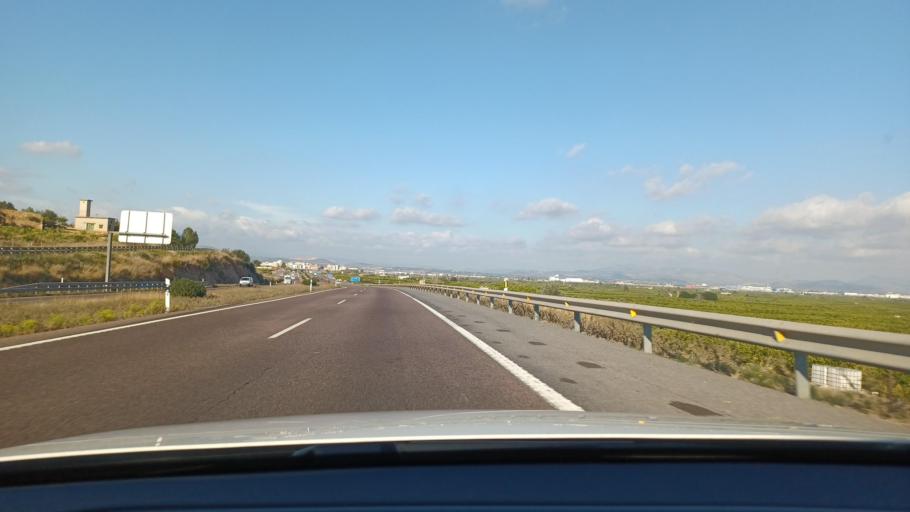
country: ES
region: Valencia
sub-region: Provincia de Castello
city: Betxi
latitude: 39.9061
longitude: -0.1955
